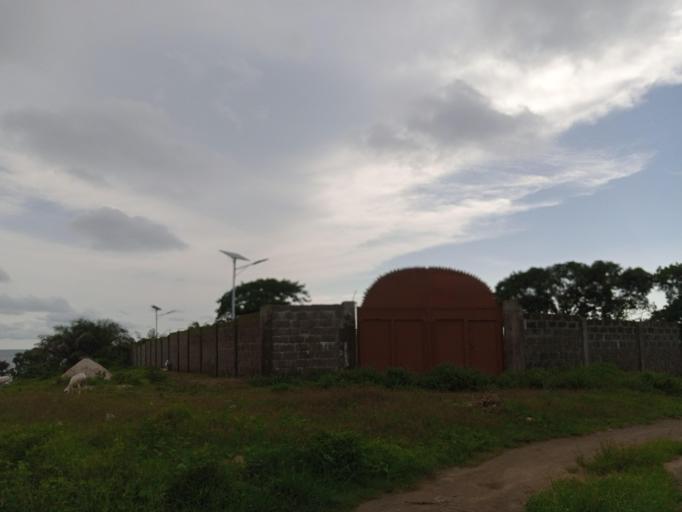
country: SL
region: Northern Province
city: Masoyila
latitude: 8.6004
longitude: -13.2030
